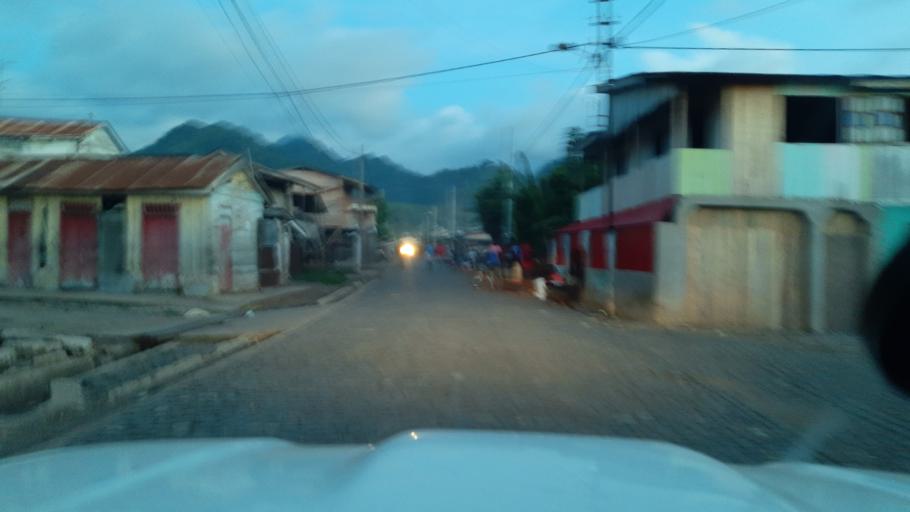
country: ST
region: Sao Tome Island
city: Sao Tome
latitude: 0.3599
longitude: 6.5475
